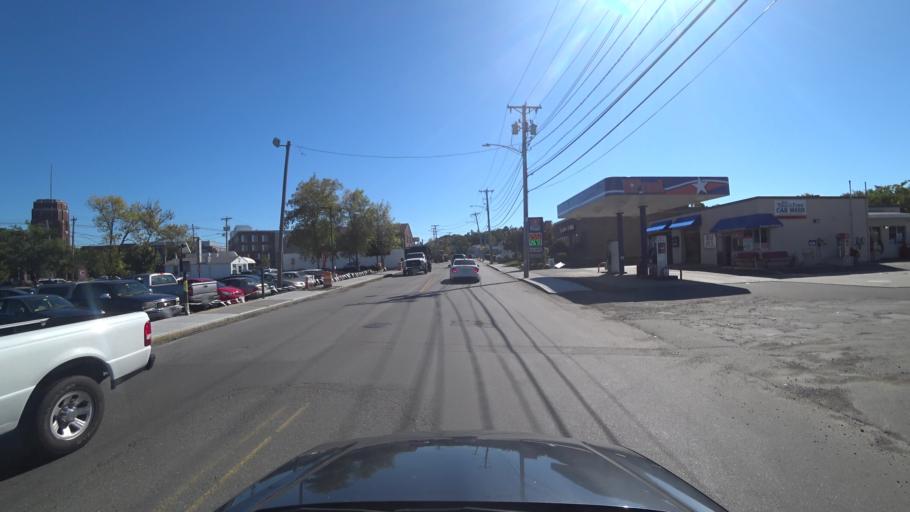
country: US
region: Massachusetts
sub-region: Essex County
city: Salem
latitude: 42.5019
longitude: -70.8960
